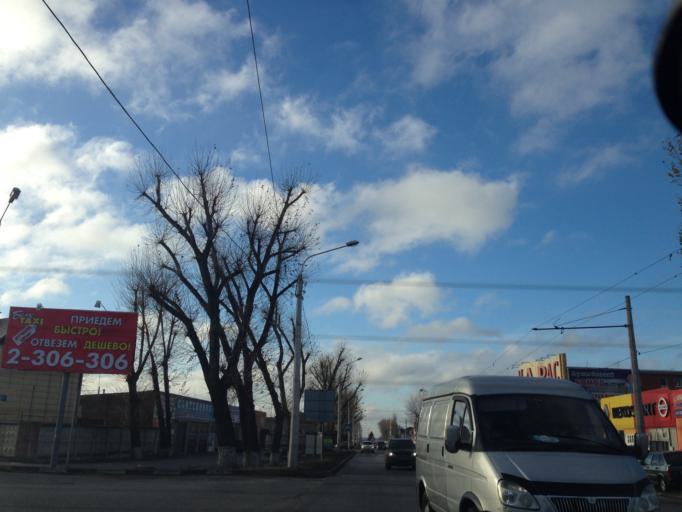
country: RU
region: Rostov
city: Severnyy
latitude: 47.2590
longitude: 39.6275
